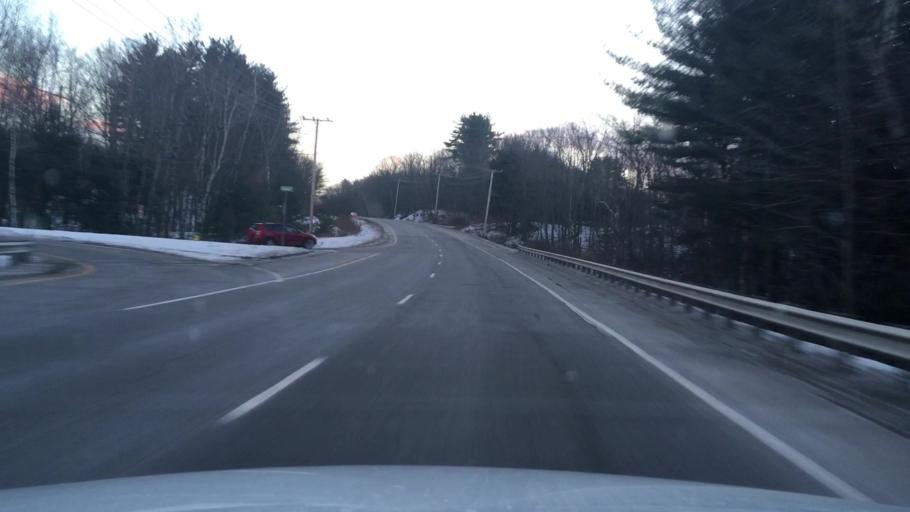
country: US
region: Maine
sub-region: Androscoggin County
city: Auburn
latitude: 44.0587
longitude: -70.2561
